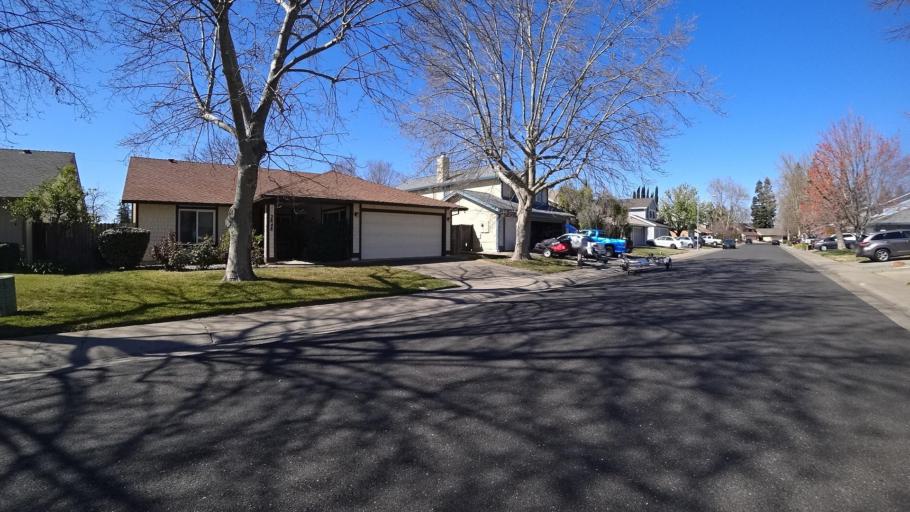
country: US
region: California
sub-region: Sacramento County
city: Rancho Cordova
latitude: 38.5793
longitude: -121.3244
